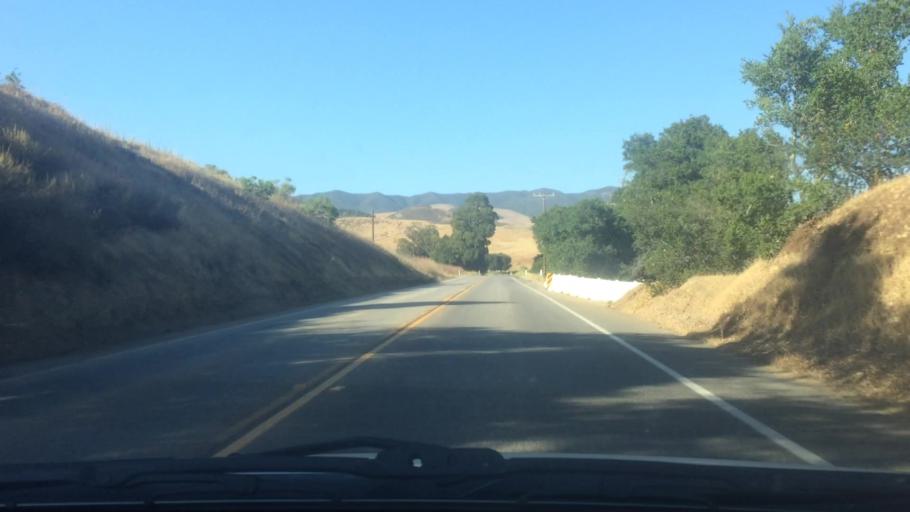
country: US
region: California
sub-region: San Luis Obispo County
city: Morro Bay
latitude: 35.4076
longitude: -120.8135
